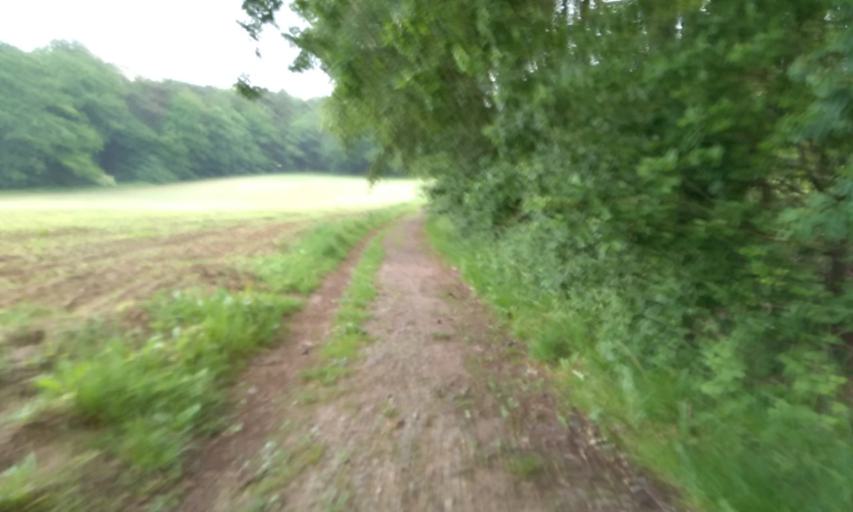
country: DE
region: Lower Saxony
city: Buxtehude
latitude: 53.4669
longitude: 9.6556
